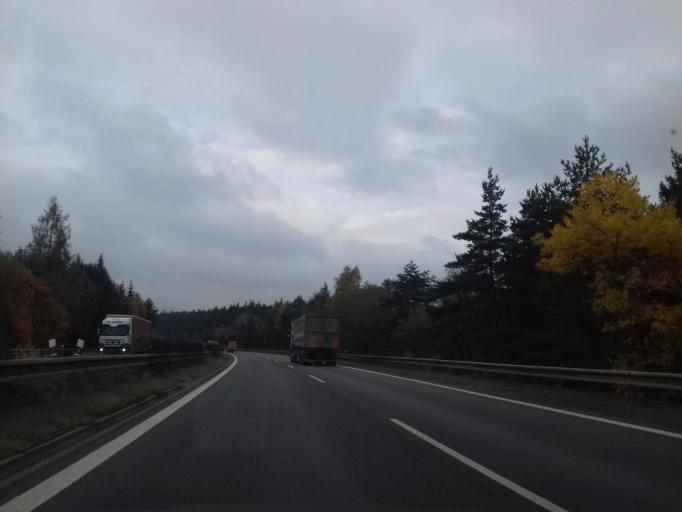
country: CZ
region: Central Bohemia
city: Zruc nad Sazavou
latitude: 49.6819
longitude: 15.1132
